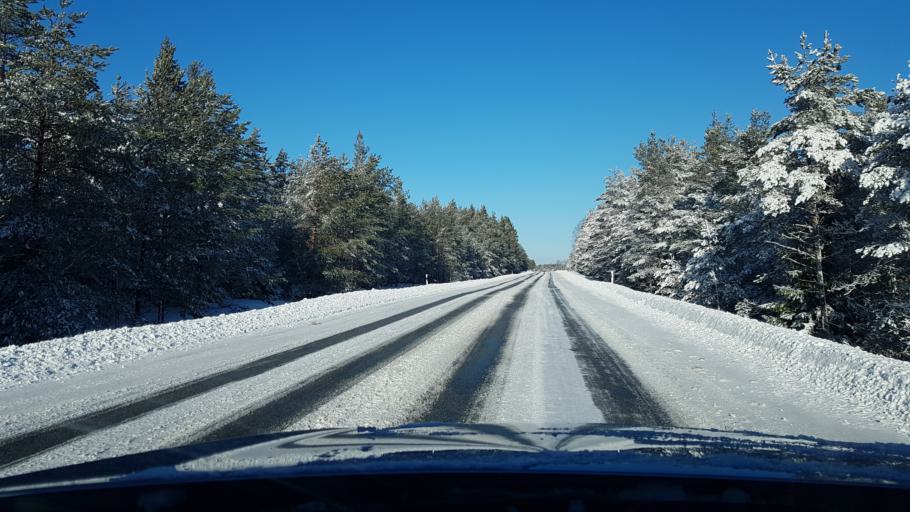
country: EE
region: Hiiumaa
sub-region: Kaerdla linn
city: Kardla
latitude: 58.9486
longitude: 22.7716
